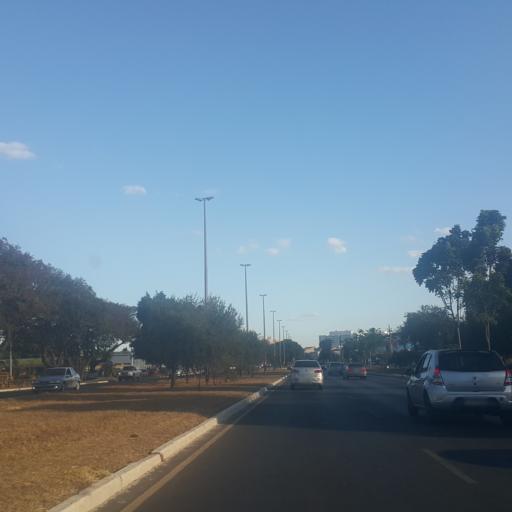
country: BR
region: Federal District
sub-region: Brasilia
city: Brasilia
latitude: -15.8298
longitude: -47.9743
